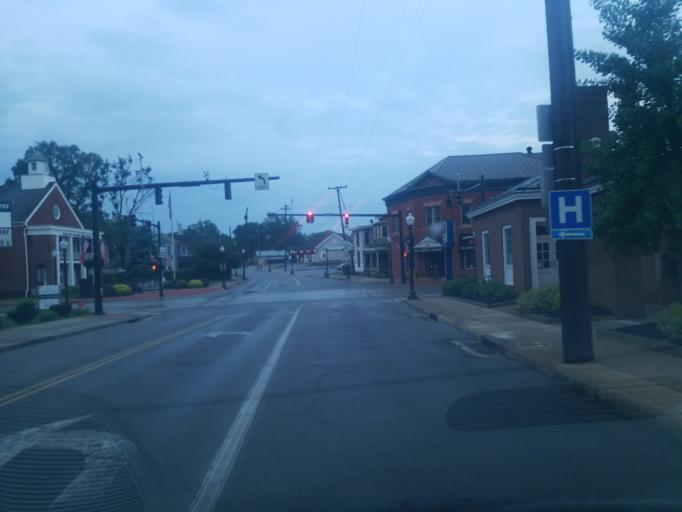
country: US
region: Ohio
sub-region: Columbiana County
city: Salem
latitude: 40.9013
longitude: -80.8516
